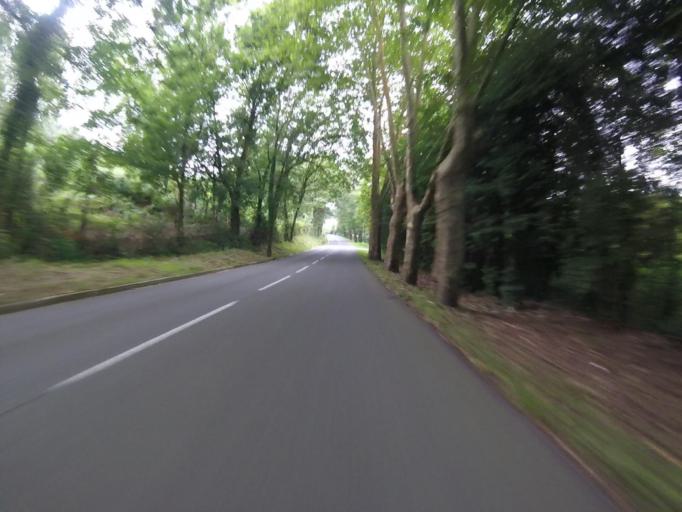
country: ES
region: Basque Country
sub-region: Provincia de Guipuzcoa
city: Irun
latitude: 43.3144
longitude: -1.8073
